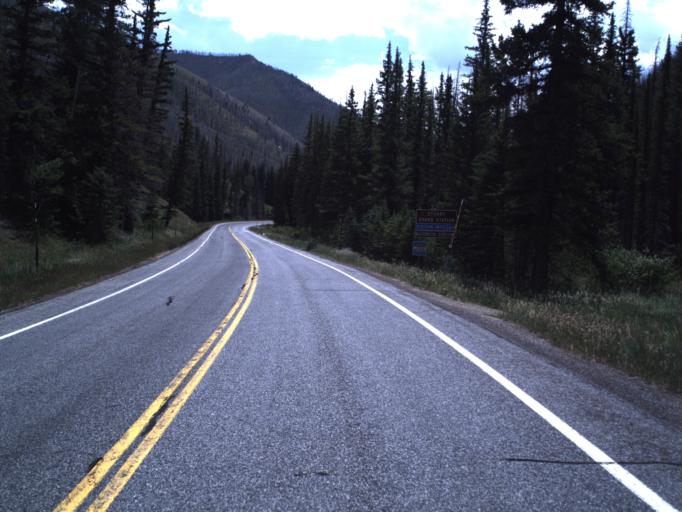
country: US
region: Utah
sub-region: Emery County
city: Huntington
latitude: 39.5346
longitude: -111.1562
